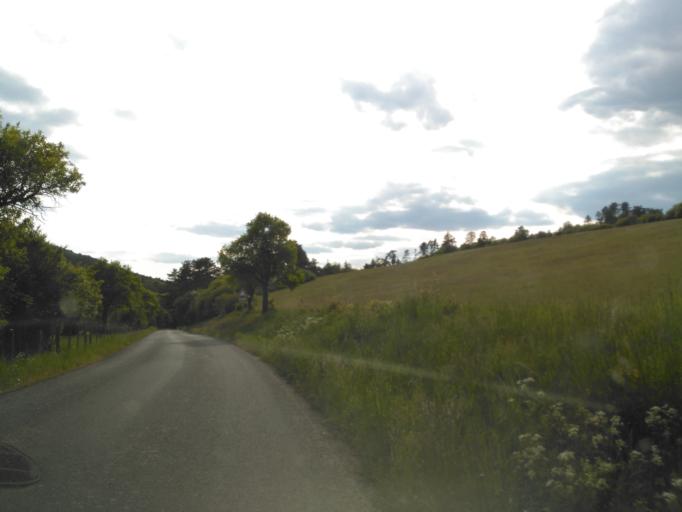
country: CZ
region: Central Bohemia
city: Zdice
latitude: 49.9149
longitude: 14.0154
